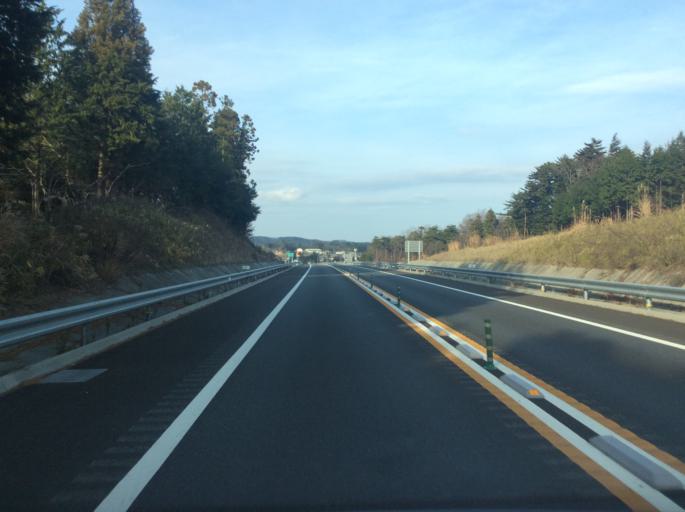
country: JP
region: Fukushima
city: Namie
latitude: 37.5515
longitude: 140.9444
